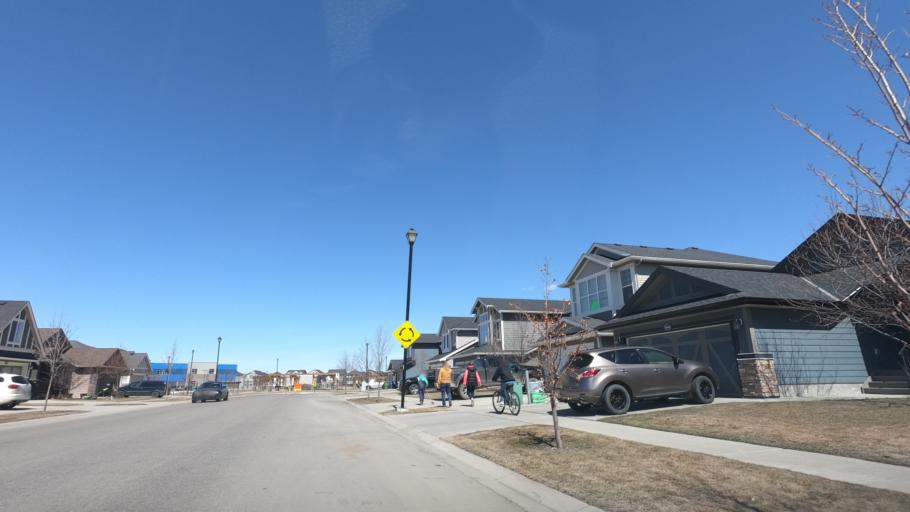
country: CA
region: Alberta
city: Airdrie
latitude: 51.3020
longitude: -114.0334
